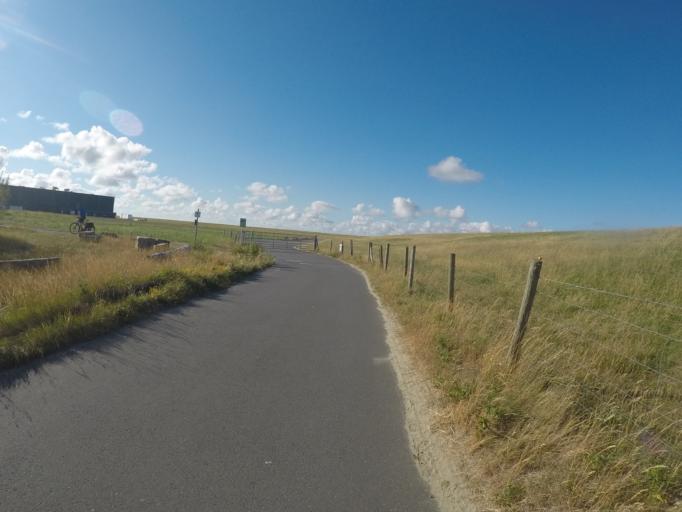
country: DE
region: Lower Saxony
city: Cuxhaven
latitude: 53.8378
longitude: 8.7684
